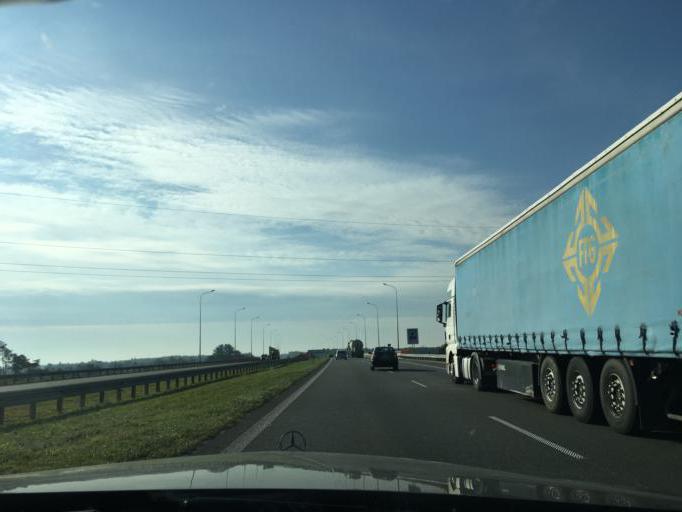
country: PL
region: Lodz Voivodeship
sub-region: Powiat lodzki wschodni
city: Andrespol
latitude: 51.7534
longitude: 19.5953
